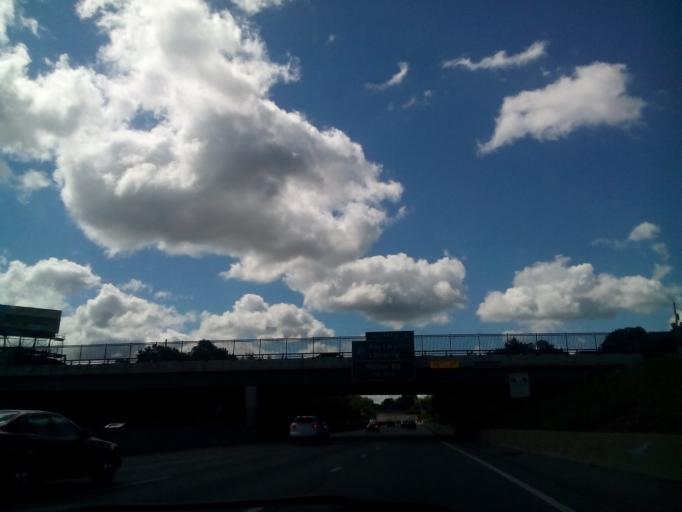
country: US
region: Michigan
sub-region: Genesee County
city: Flint
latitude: 43.0028
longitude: -83.7496
